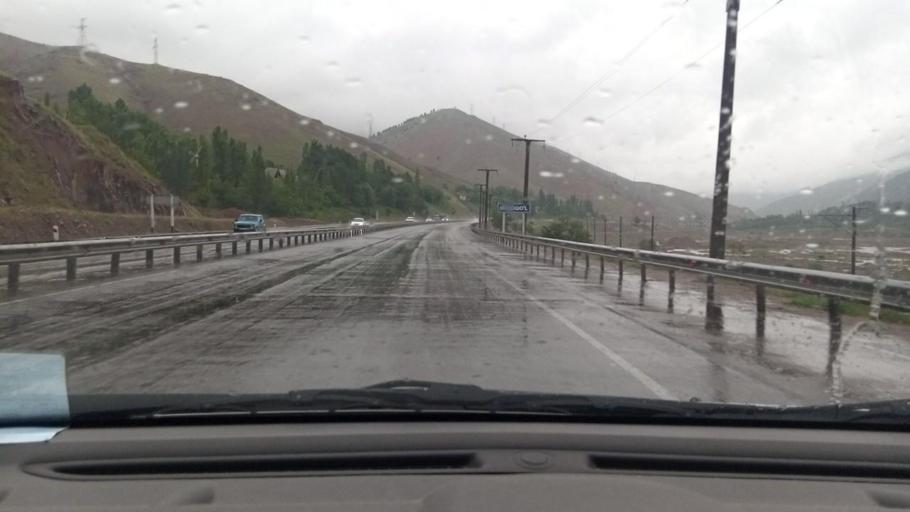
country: UZ
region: Toshkent
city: Angren
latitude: 41.1416
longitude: 70.4019
